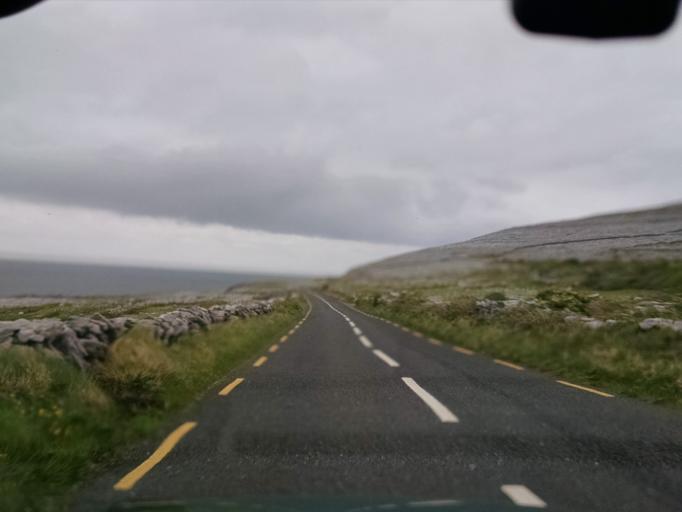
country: IE
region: Connaught
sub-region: County Galway
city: Bearna
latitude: 53.1451
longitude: -9.2728
